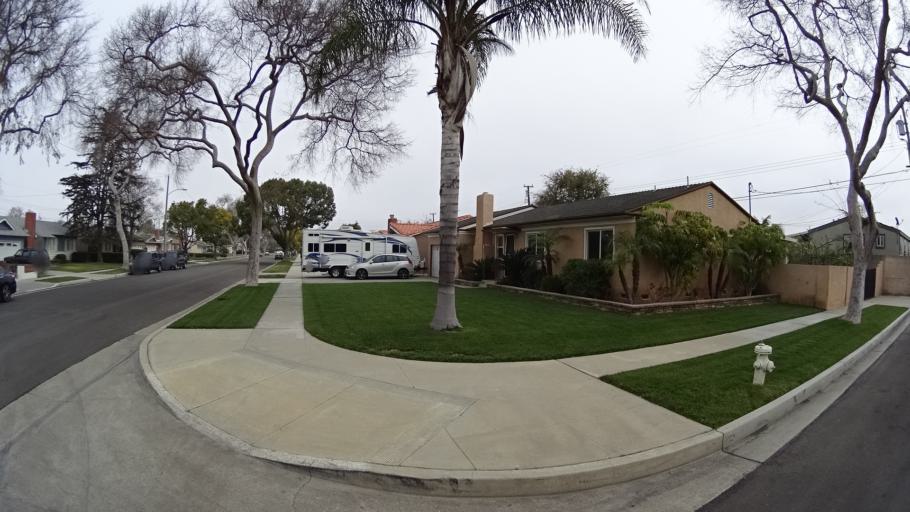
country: US
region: California
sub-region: Orange County
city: Stanton
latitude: 33.8151
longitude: -117.9980
